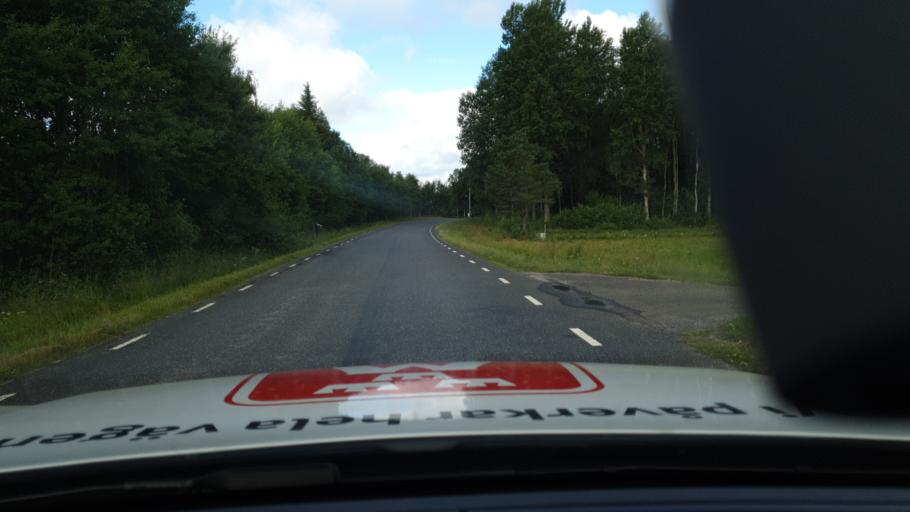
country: SE
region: Vaestra Goetaland
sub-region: Falkopings Kommun
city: Floby
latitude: 58.1254
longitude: 13.3940
